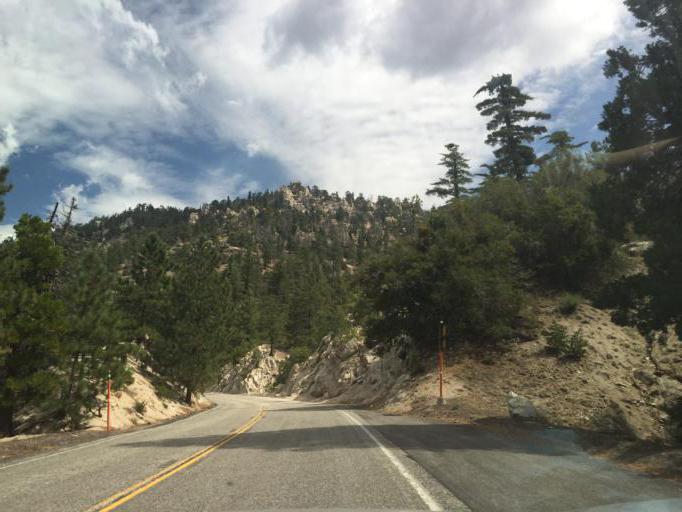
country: US
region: California
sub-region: Los Angeles County
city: Littlerock
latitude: 34.3425
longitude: -117.9758
